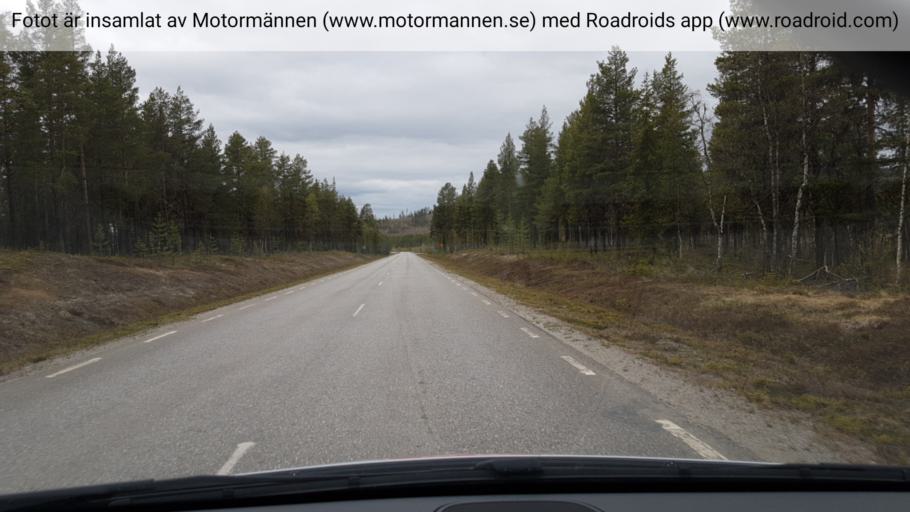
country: SE
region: Vaesterbotten
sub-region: Sorsele Kommun
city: Sorsele
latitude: 65.5443
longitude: 17.4132
